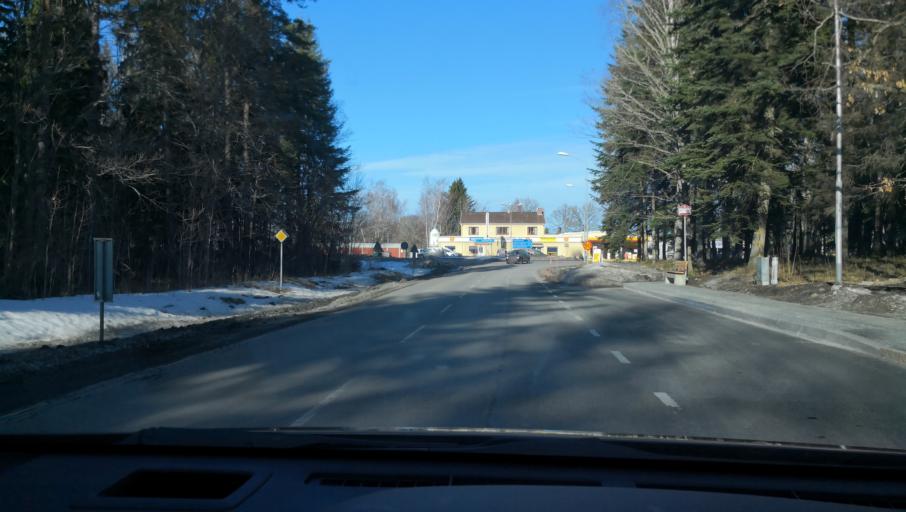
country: SE
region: Uppsala
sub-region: Osthammars Kommun
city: Osterbybruk
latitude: 60.1965
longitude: 17.8781
